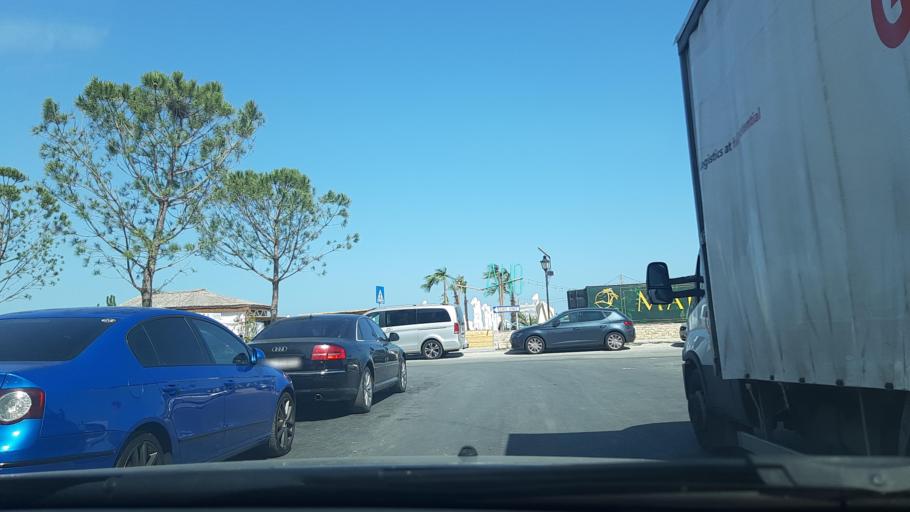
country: RO
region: Constanta
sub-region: Comuna Navodari
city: Navodari
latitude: 44.3057
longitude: 28.6279
